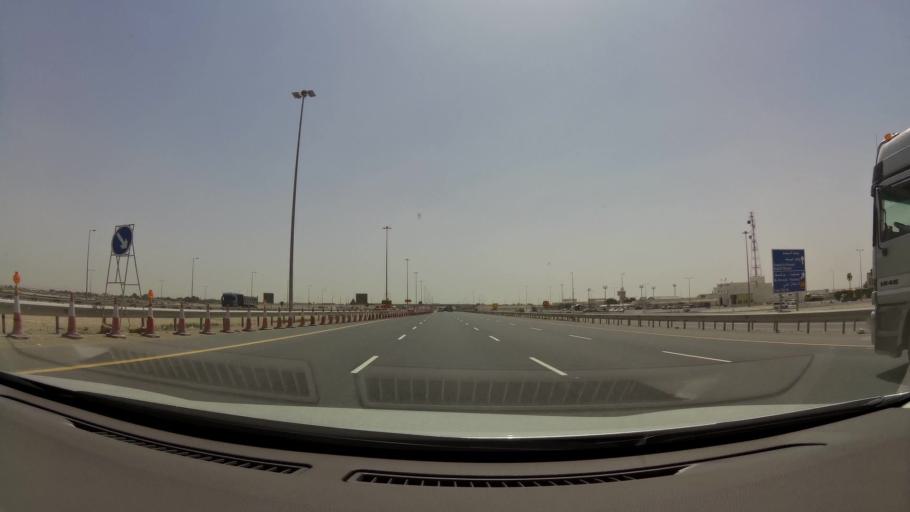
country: QA
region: Baladiyat Umm Salal
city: Umm Salal `Ali
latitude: 25.4553
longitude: 51.4092
